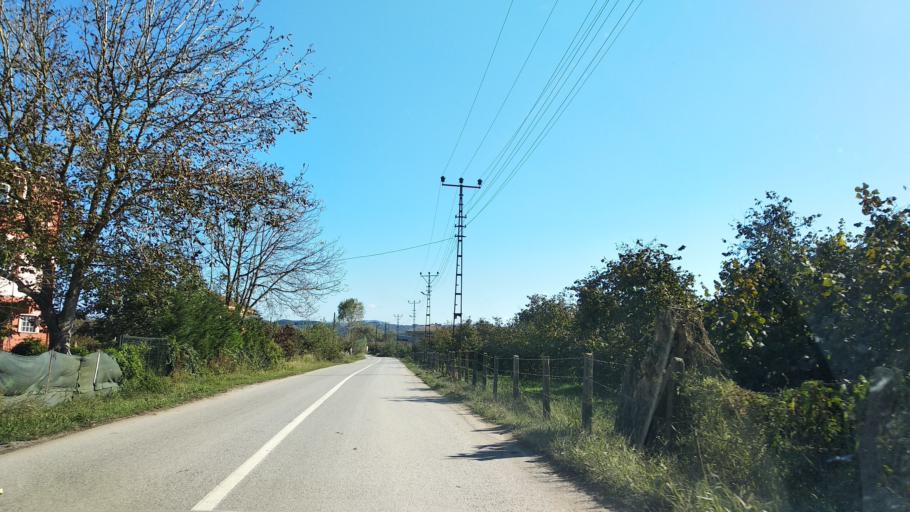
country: TR
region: Sakarya
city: Ortakoy
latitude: 41.0265
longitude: 30.5972
